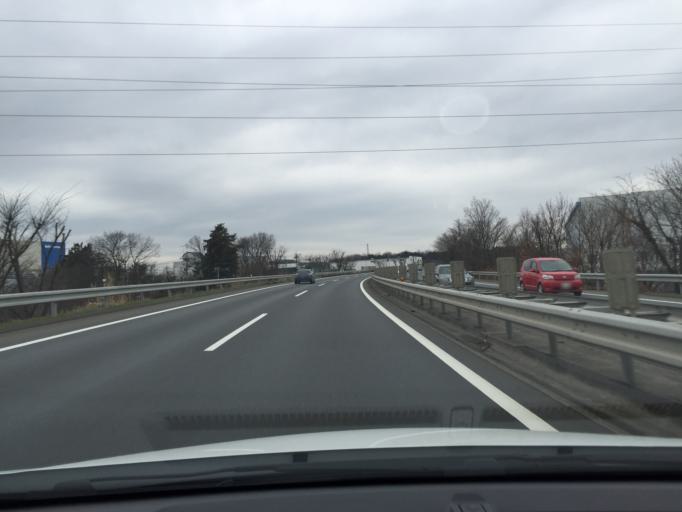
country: JP
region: Saitama
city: Sayama
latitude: 35.8850
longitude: 139.3874
